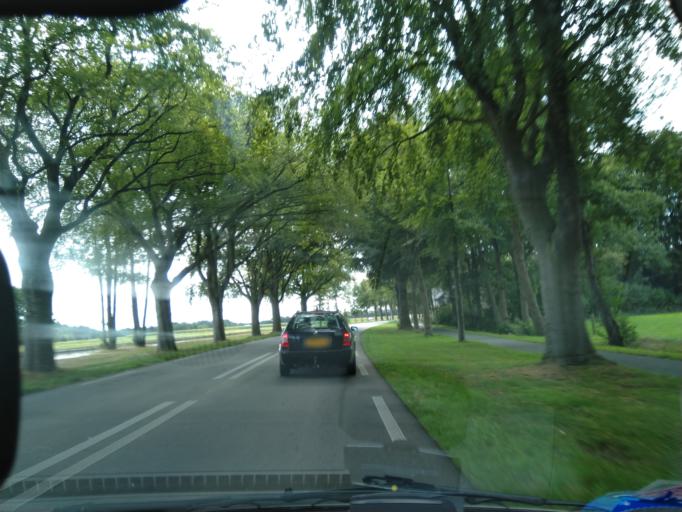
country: NL
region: Drenthe
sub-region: Gemeente Tynaarlo
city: Tynaarlo
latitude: 53.1058
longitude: 6.6046
